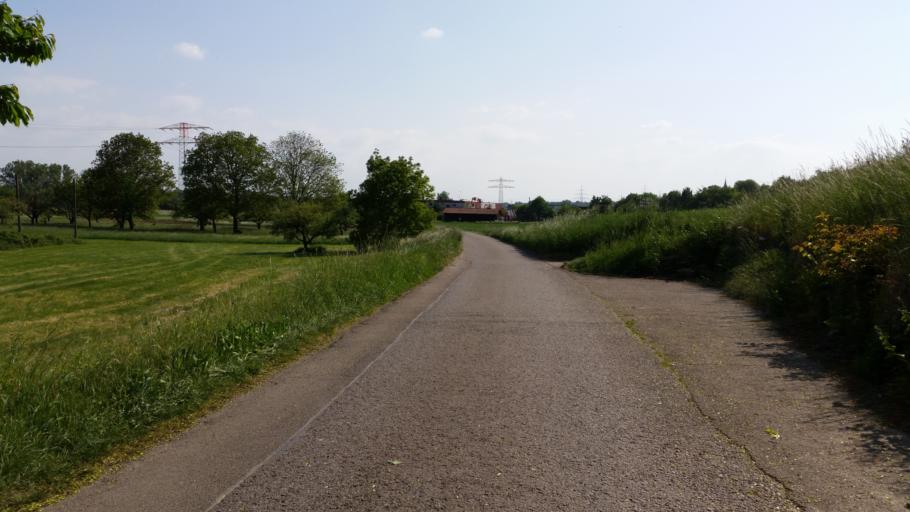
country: DE
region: Baden-Wuerttemberg
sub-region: Regierungsbezirk Stuttgart
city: Pleidelsheim
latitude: 48.9673
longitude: 9.1941
